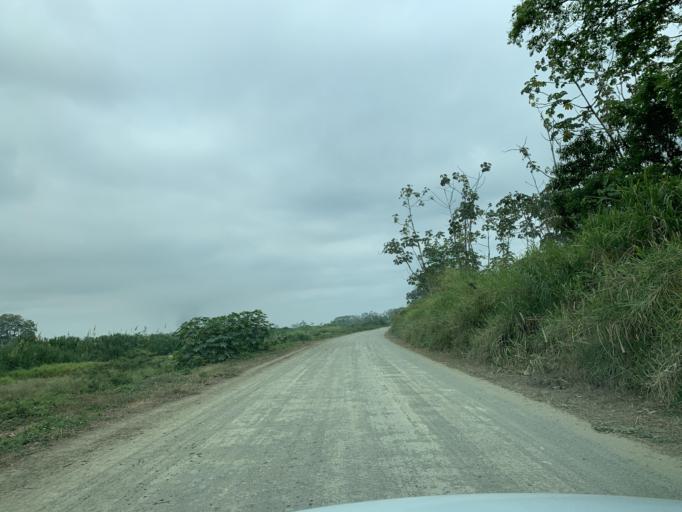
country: EC
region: Canar
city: La Troncal
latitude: -2.3616
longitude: -79.4632
